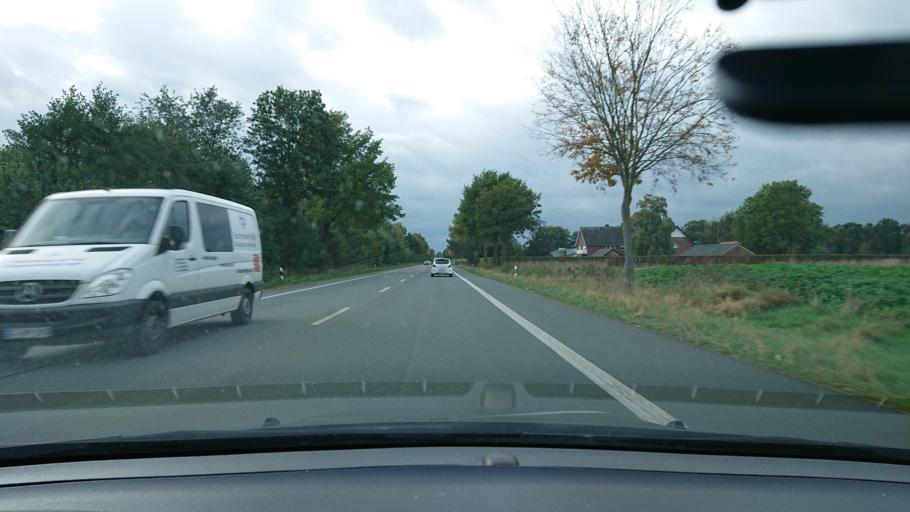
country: DE
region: North Rhine-Westphalia
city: Rietberg
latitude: 51.7440
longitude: 8.4261
